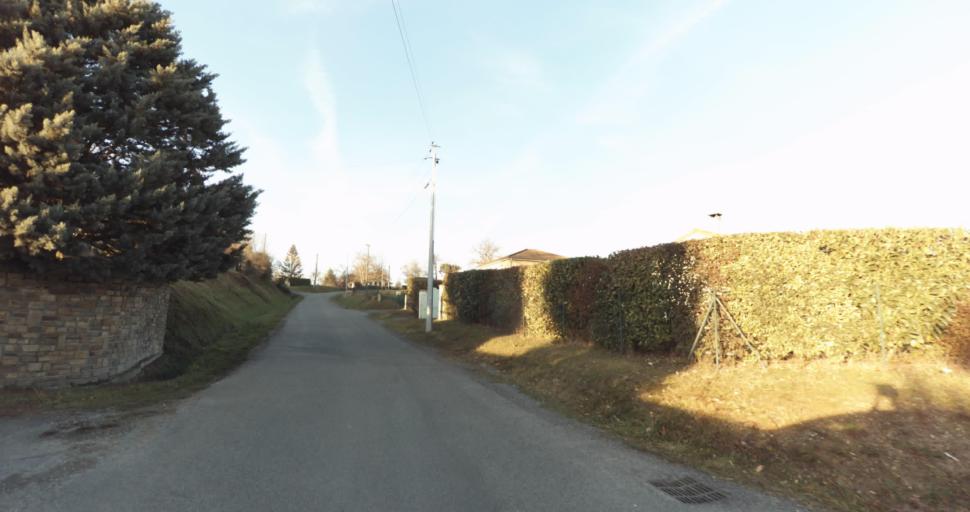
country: FR
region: Limousin
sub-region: Departement de la Haute-Vienne
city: Aixe-sur-Vienne
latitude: 45.8030
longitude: 1.1276
